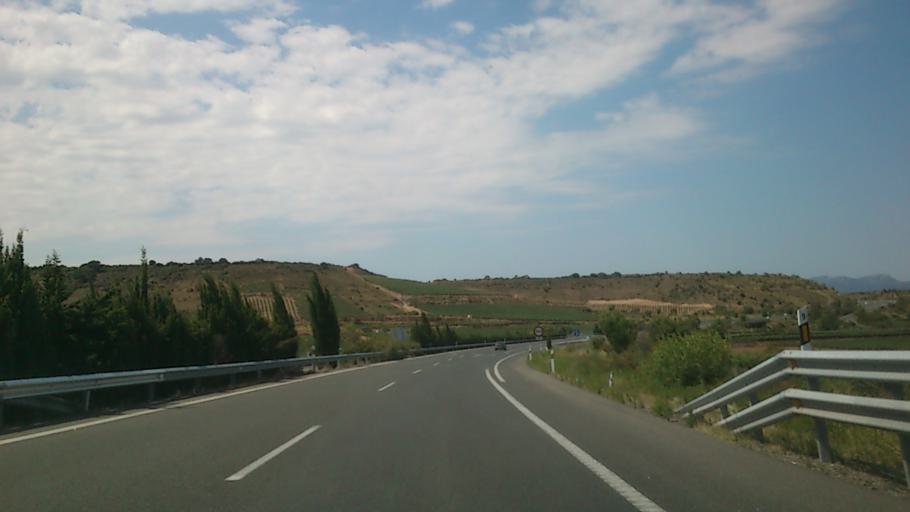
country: ES
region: La Rioja
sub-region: Provincia de La Rioja
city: Cenicero
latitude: 42.4632
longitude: -2.6413
